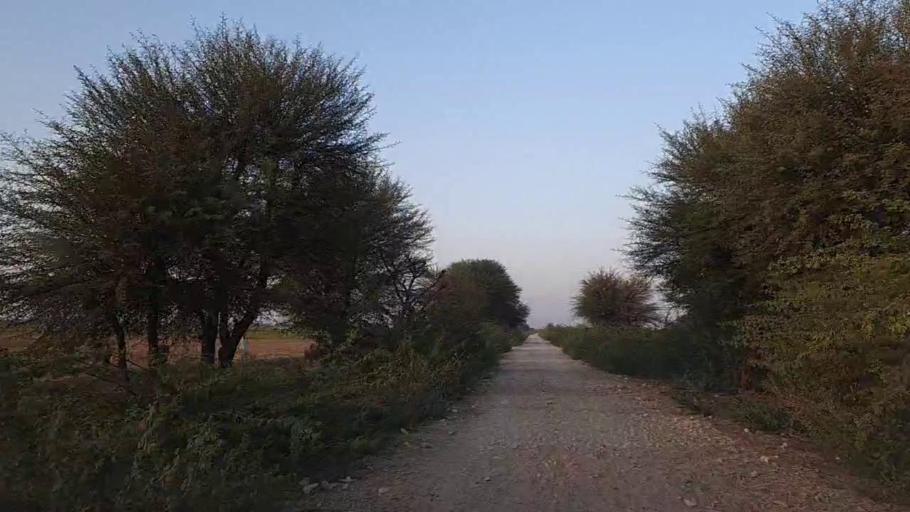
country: PK
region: Sindh
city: Naukot
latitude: 24.8733
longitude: 69.3489
